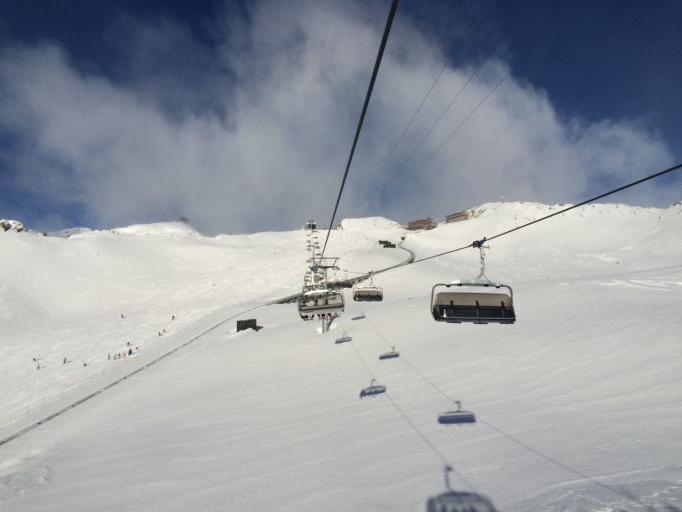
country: CH
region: Grisons
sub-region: Praettigau/Davos District
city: Davos
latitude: 46.8280
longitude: 9.8105
